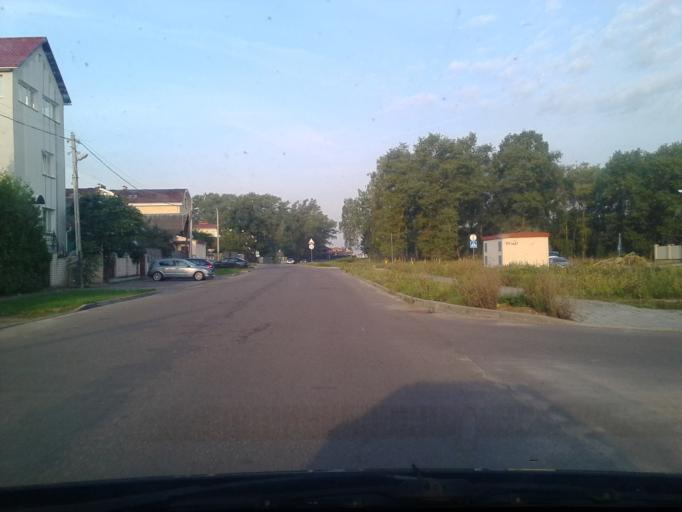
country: BY
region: Minsk
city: Minsk
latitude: 53.9511
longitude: 27.5870
